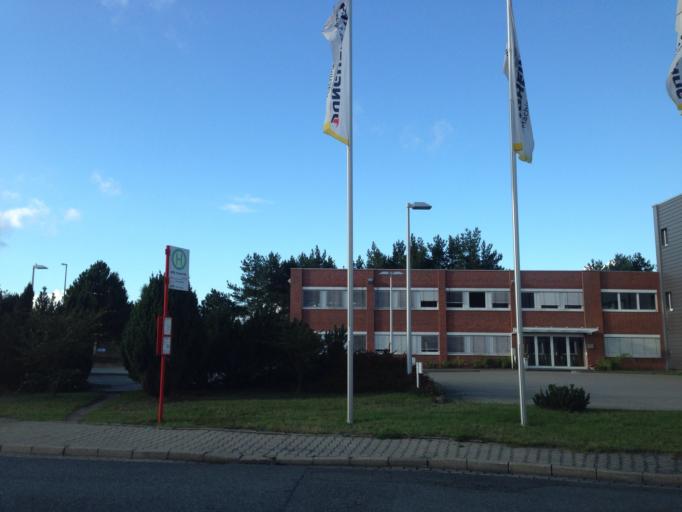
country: DE
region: Lower Saxony
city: Wendisch Evern
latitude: 53.2389
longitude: 10.4761
